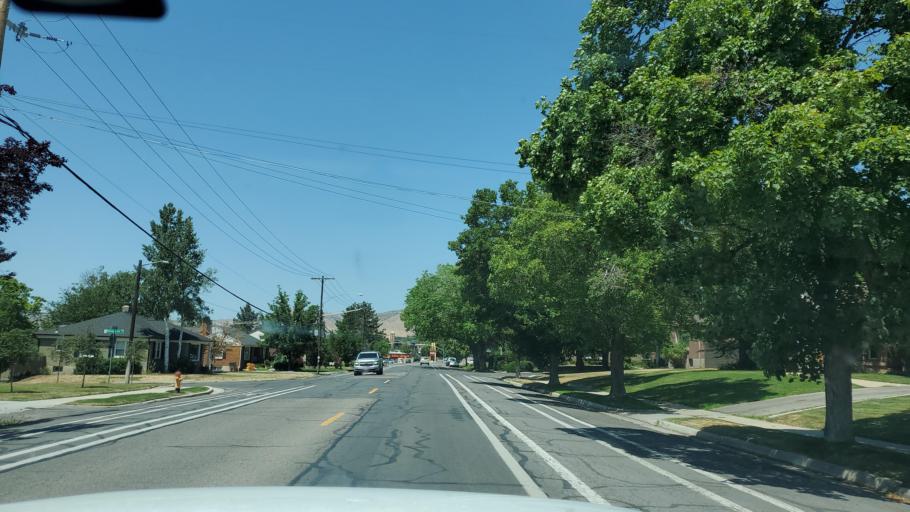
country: US
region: Utah
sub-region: Salt Lake County
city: Canyon Rim
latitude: 40.7229
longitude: -111.8245
